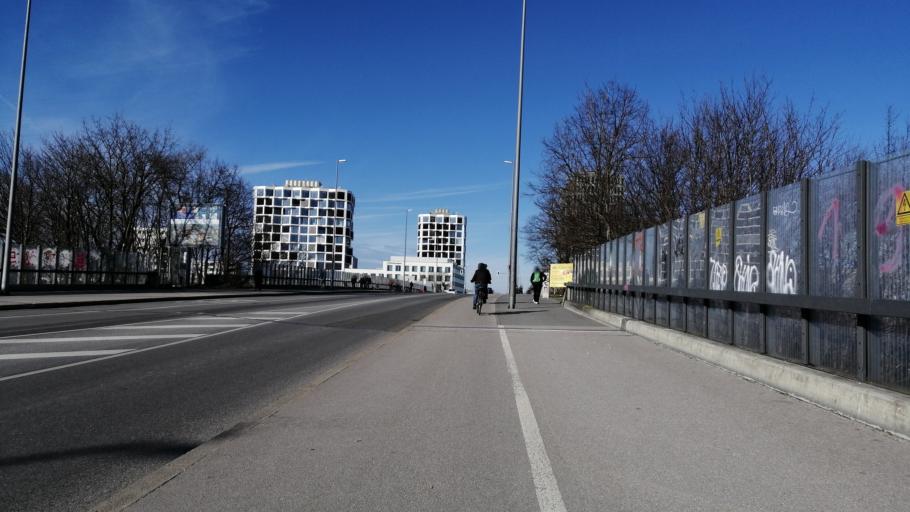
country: DE
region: Bavaria
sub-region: Upper Bavaria
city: Munich
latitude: 48.1420
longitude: 11.5191
